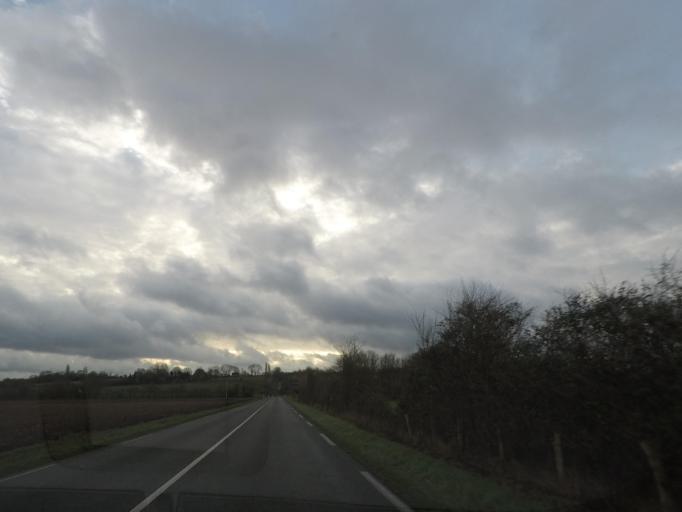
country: FR
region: Pays de la Loire
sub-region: Departement de la Sarthe
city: Cherre
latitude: 48.1271
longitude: 0.7023
